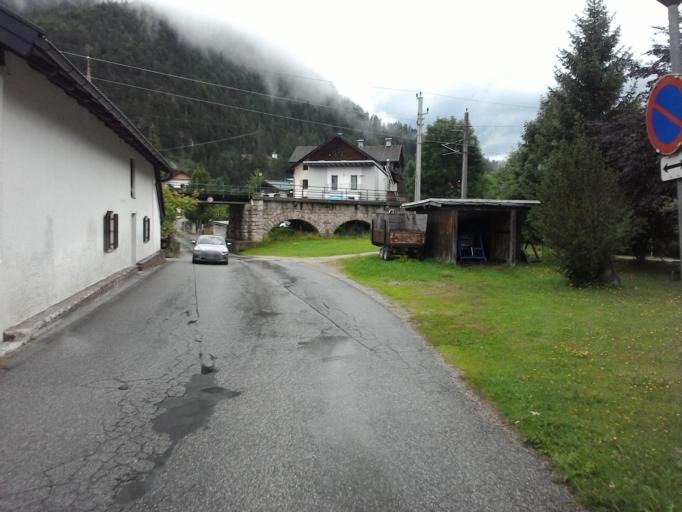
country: AT
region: Tyrol
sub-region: Politischer Bezirk Innsbruck Land
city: Scharnitz
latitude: 47.3879
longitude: 11.2650
